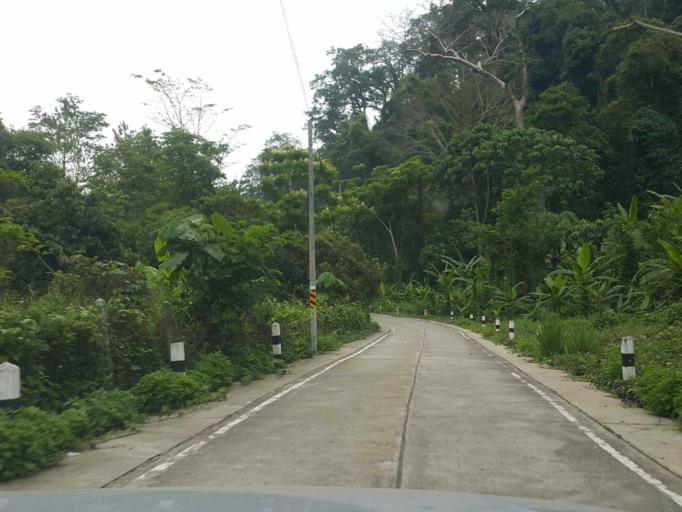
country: TH
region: Chiang Mai
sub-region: Amphoe Chiang Dao
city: Chiang Dao
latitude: 19.4121
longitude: 98.9214
